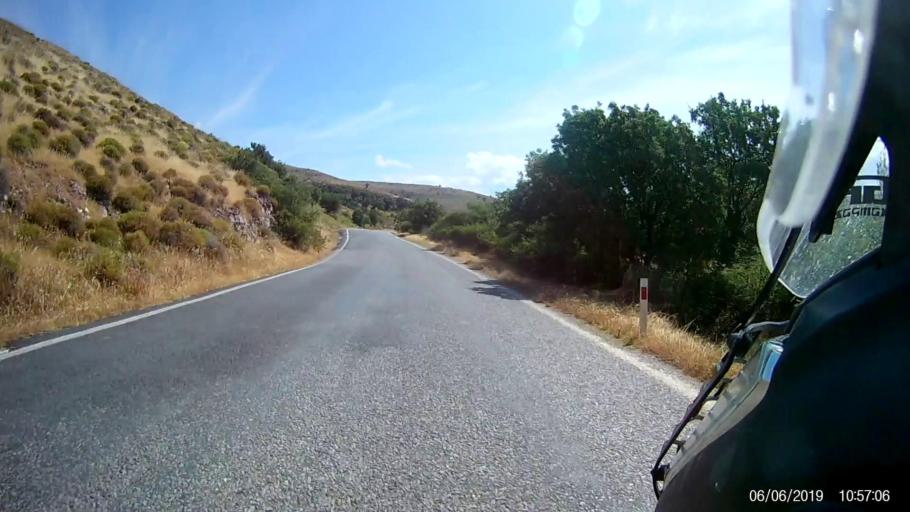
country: TR
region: Canakkale
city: Ayvacik
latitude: 39.5250
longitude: 26.4737
